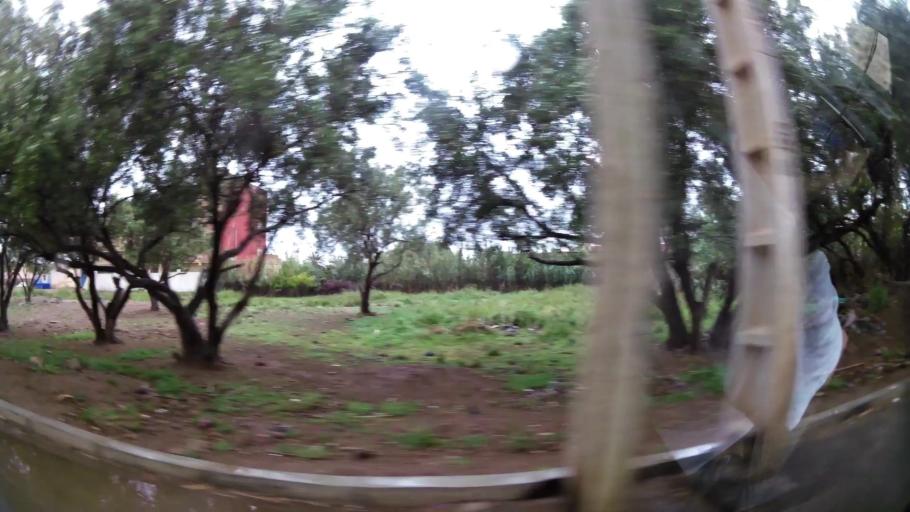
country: MA
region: Oriental
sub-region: Nador
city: Nador
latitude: 35.1567
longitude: -2.9517
